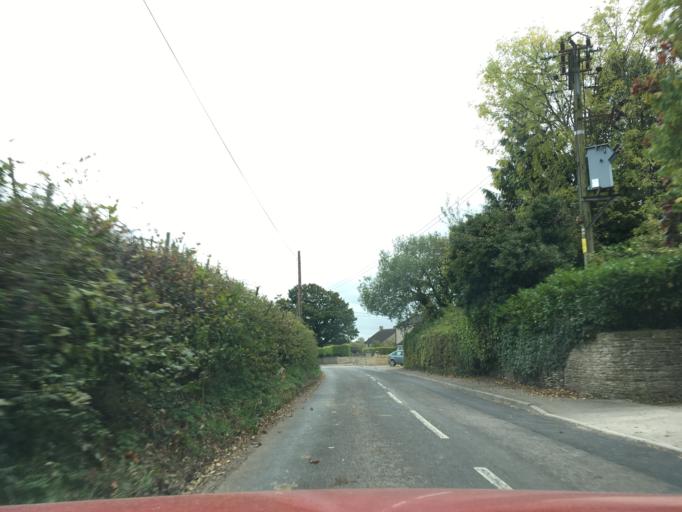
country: GB
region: England
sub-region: South Gloucestershire
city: Horton
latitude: 51.5769
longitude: -2.3114
